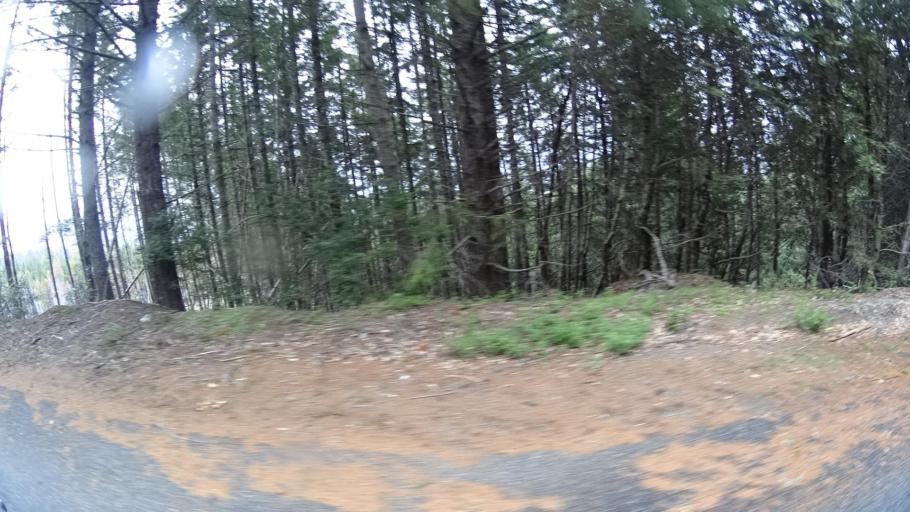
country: US
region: California
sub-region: Humboldt County
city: Willow Creek
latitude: 41.2019
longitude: -123.7868
